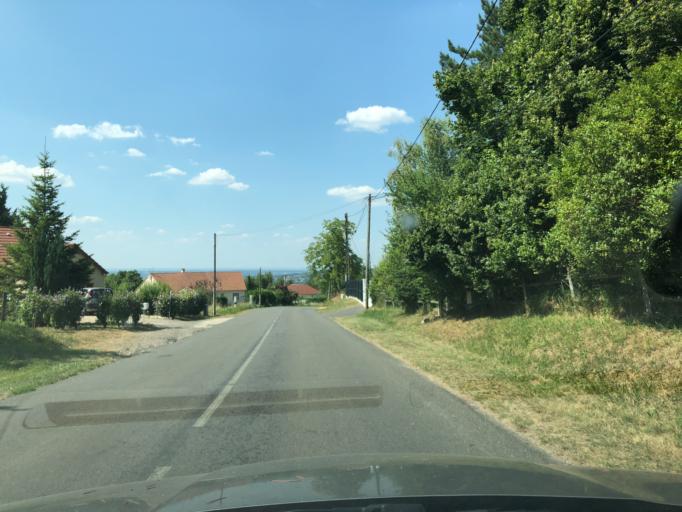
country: FR
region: Auvergne
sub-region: Departement de l'Allier
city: Cusset
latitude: 46.1129
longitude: 3.4626
